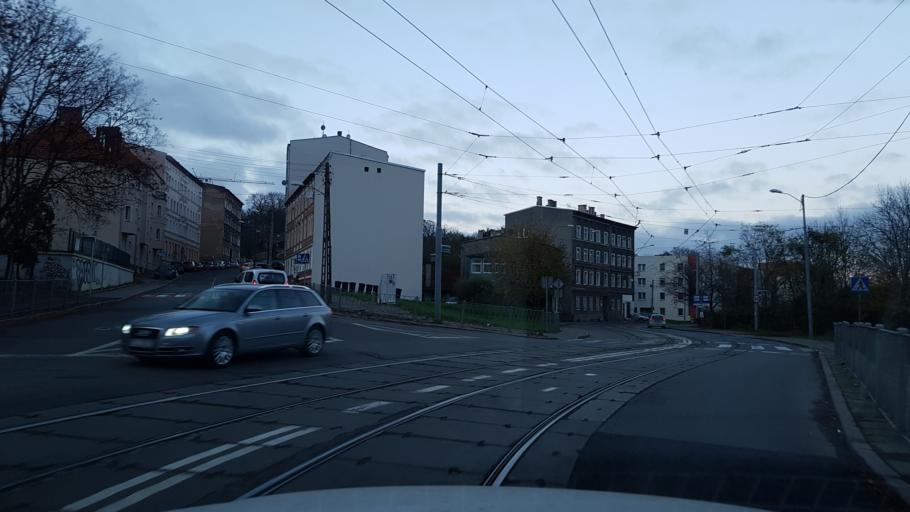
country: PL
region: West Pomeranian Voivodeship
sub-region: Szczecin
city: Szczecin
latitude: 53.4627
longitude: 14.5947
